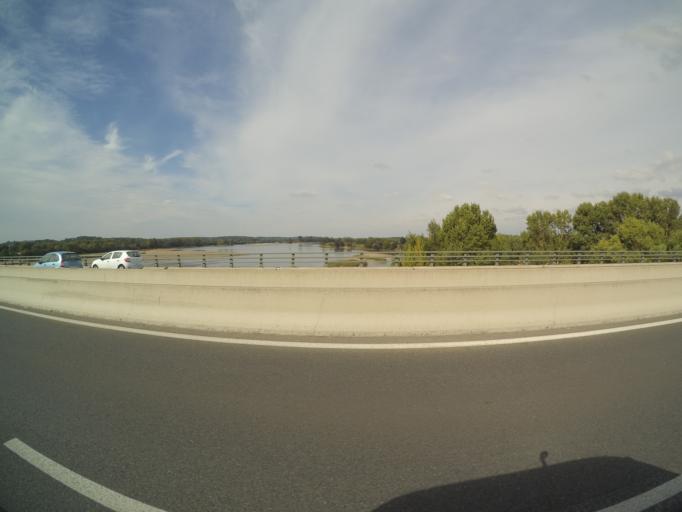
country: FR
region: Pays de la Loire
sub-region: Departement de Maine-et-Loire
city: Saumur
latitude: 47.2711
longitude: -0.0844
